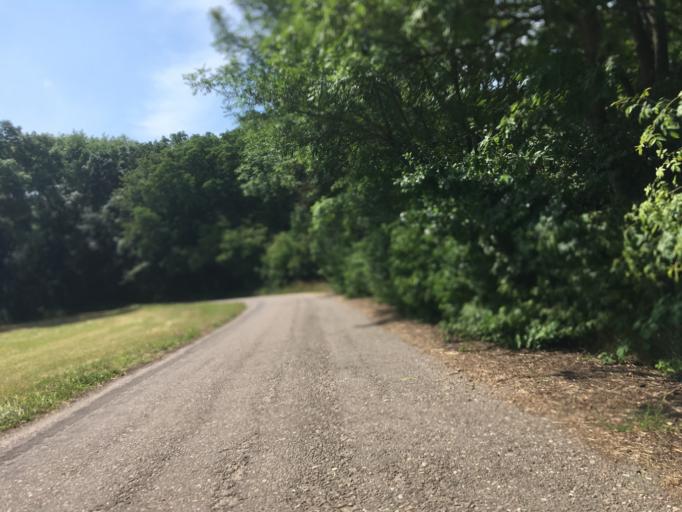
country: DE
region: Saxony-Anhalt
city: Osternienburg
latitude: 51.7553
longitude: 12.0413
